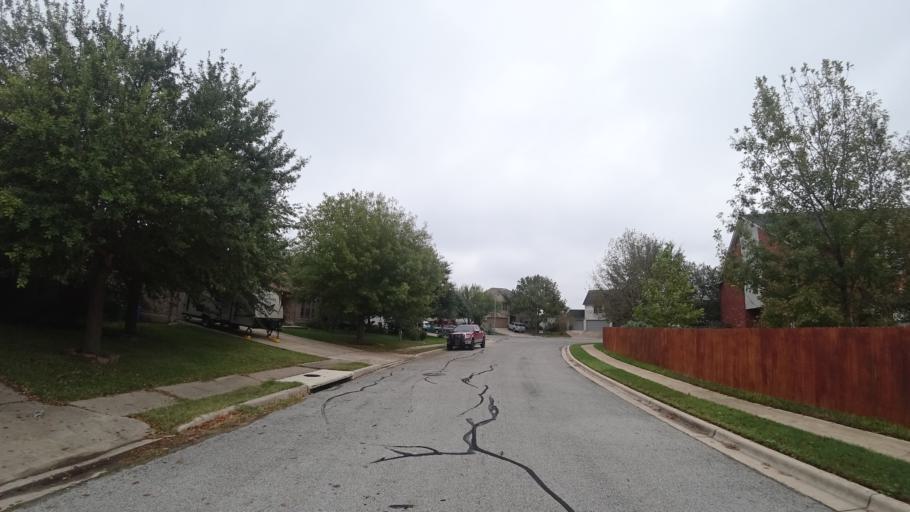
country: US
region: Texas
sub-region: Travis County
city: Pflugerville
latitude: 30.4258
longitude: -97.6198
